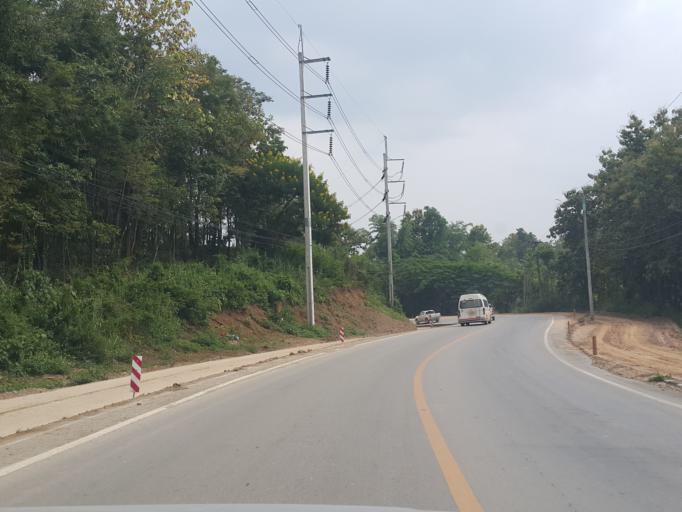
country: TH
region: Chiang Mai
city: Mae Taeng
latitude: 19.0909
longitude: 98.8645
